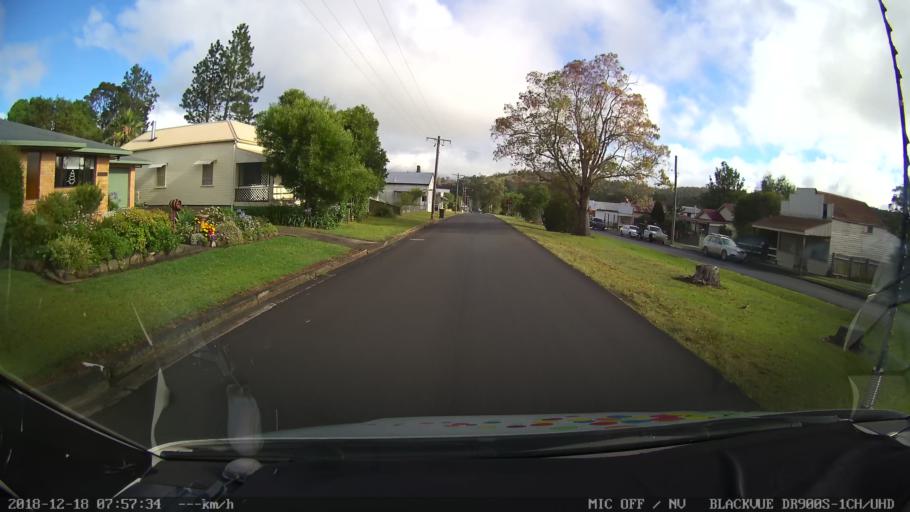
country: AU
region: New South Wales
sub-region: Kyogle
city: Kyogle
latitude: -28.3922
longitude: 152.6118
